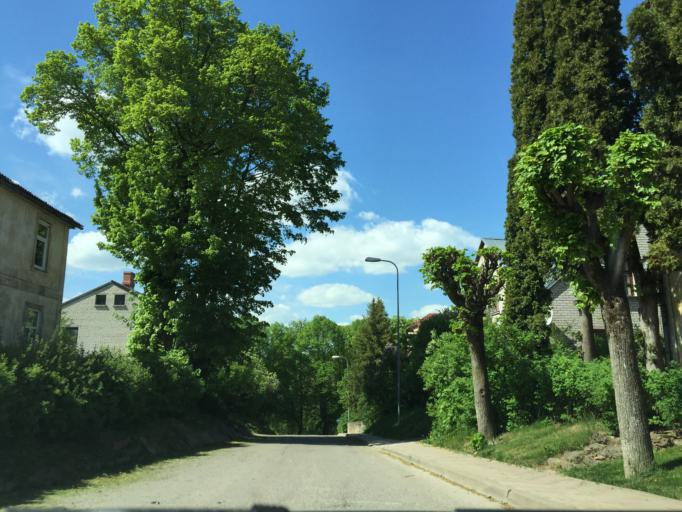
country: LV
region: Bauskas Rajons
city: Bauska
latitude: 56.4055
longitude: 24.1811
